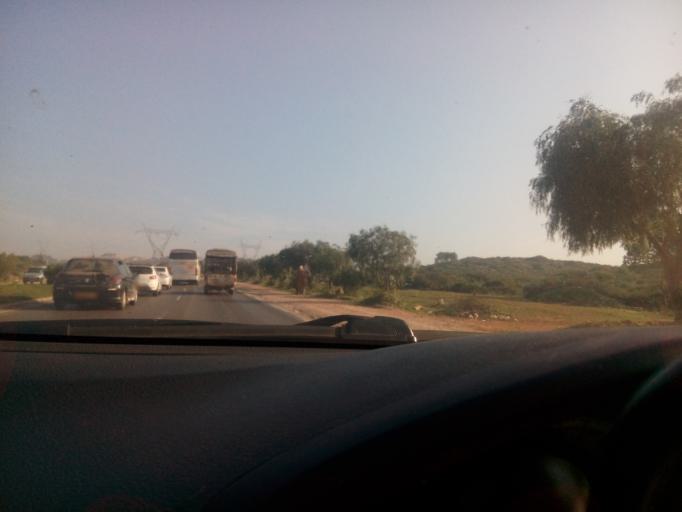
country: DZ
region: Oran
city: Oran
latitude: 35.6378
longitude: -0.7106
